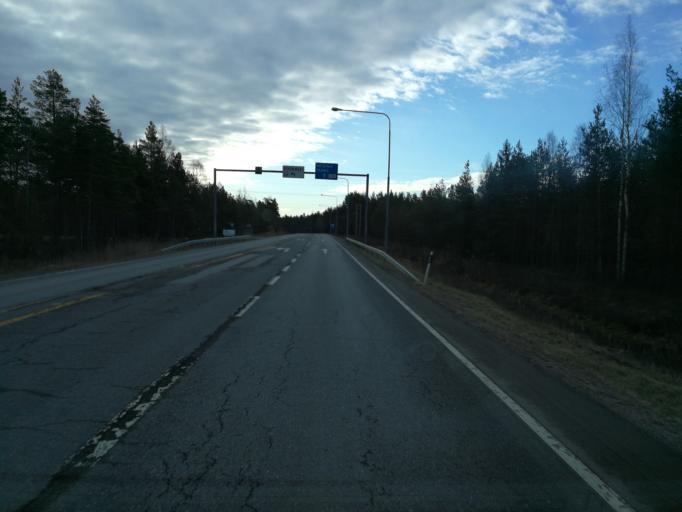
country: FI
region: Varsinais-Suomi
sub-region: Turku
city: Paimio
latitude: 60.4221
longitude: 22.7154
